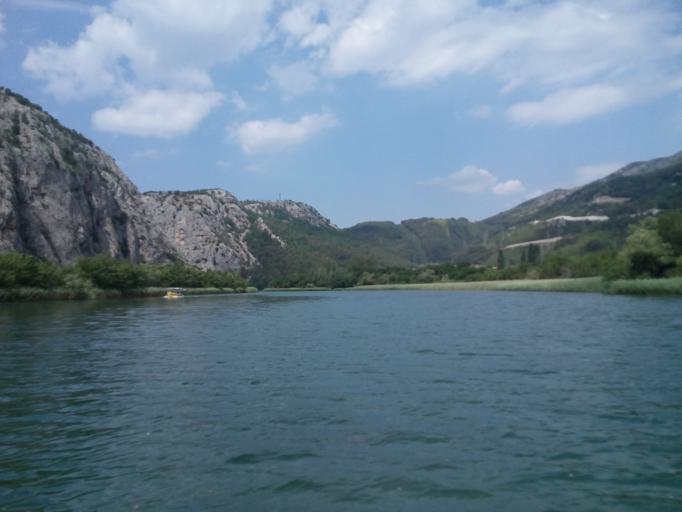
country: HR
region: Splitsko-Dalmatinska
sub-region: Grad Omis
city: Omis
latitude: 43.4506
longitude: 16.7071
